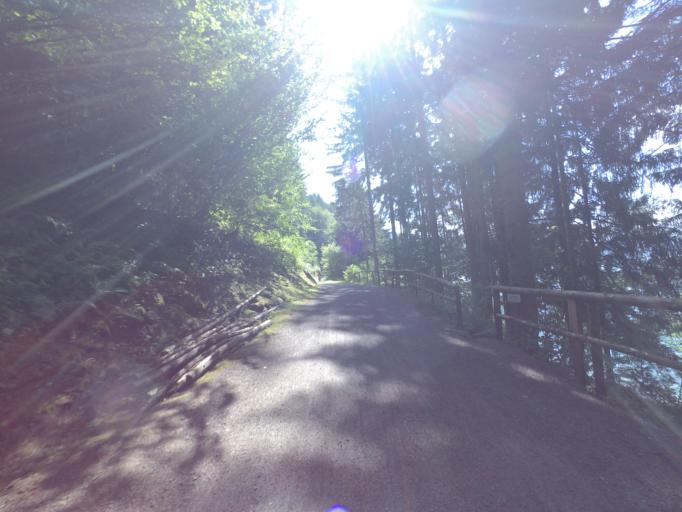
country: AT
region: Carinthia
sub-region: Politischer Bezirk Villach Land
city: Ferndorf
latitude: 46.7655
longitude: 13.6442
